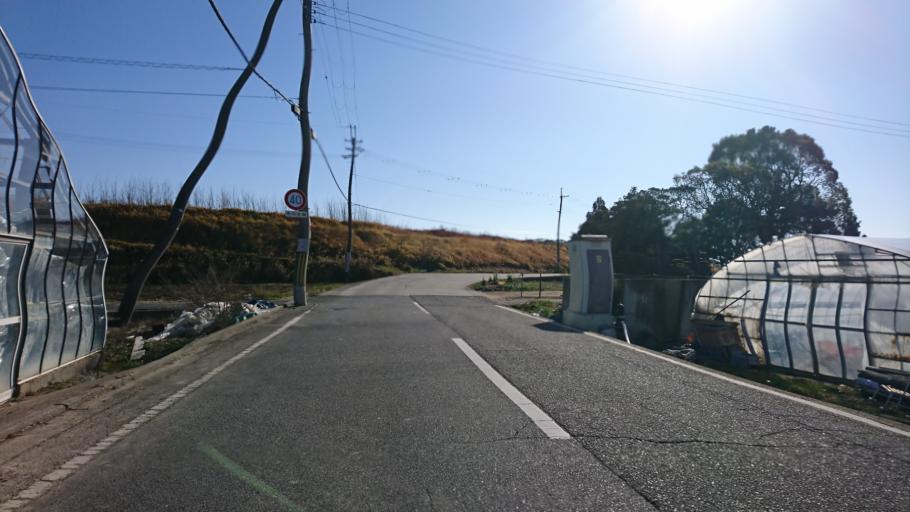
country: JP
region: Hyogo
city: Miki
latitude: 34.7263
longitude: 134.9568
